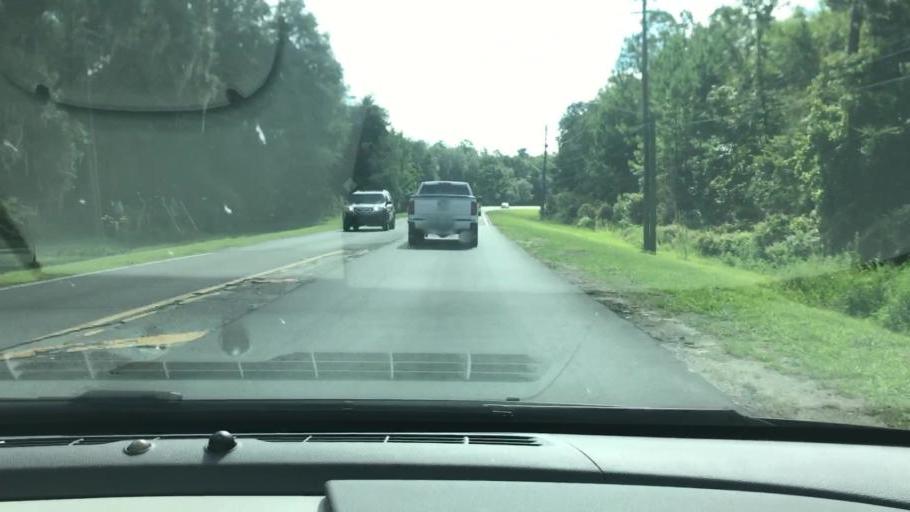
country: US
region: Florida
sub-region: Alachua County
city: Gainesville
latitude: 29.6498
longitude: -82.4063
